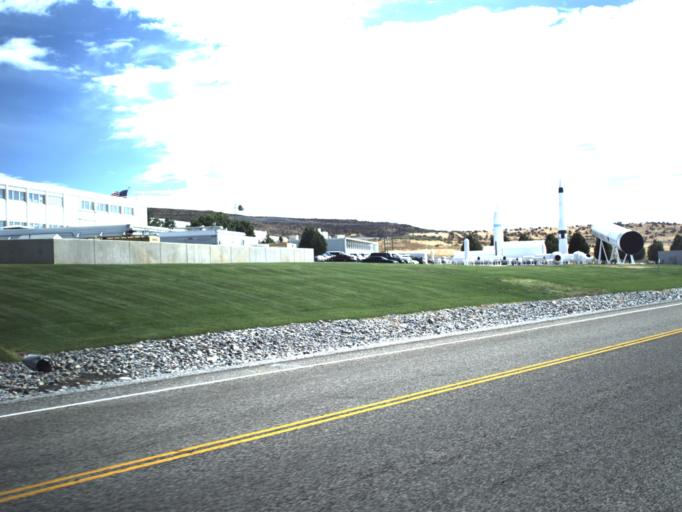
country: US
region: Utah
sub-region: Box Elder County
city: Tremonton
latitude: 41.6601
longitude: -112.4424
